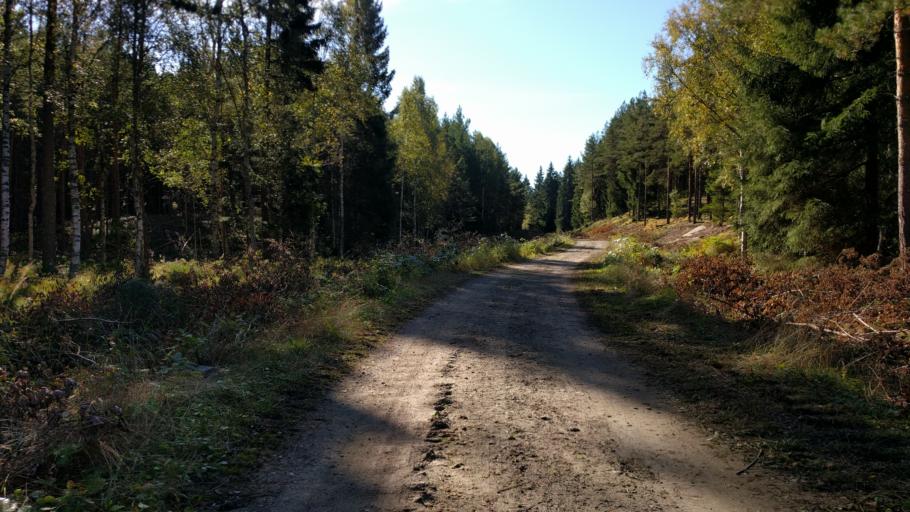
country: SE
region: Stockholm
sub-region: Vallentuna Kommun
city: Vallentuna
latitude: 59.4935
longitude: 18.1129
